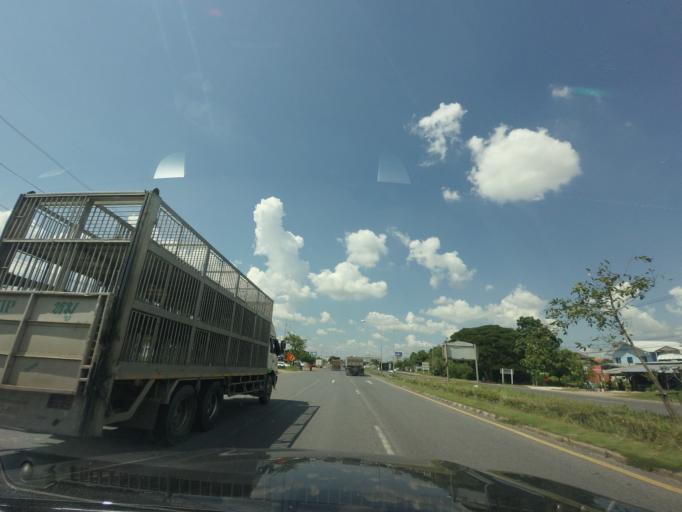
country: TH
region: Nakhon Ratchasima
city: Nakhon Ratchasima
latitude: 14.9710
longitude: 102.0522
